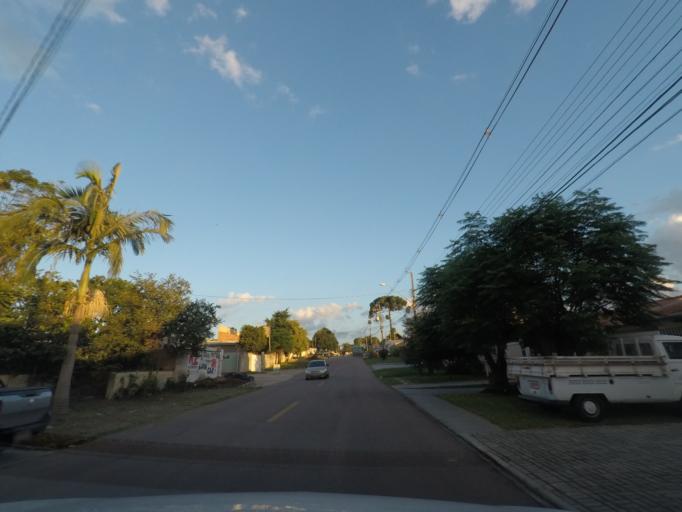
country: BR
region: Parana
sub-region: Sao Jose Dos Pinhais
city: Sao Jose dos Pinhais
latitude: -25.4981
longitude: -49.2559
